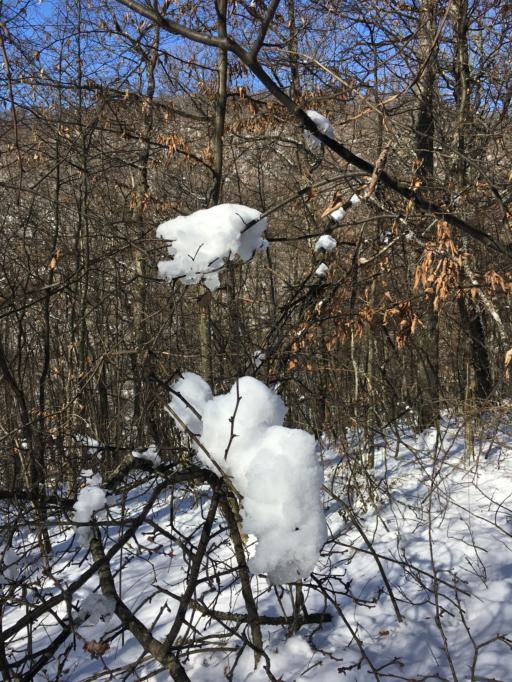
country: XK
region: Pristina
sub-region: Komuna e Prishtines
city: Pristina
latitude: 42.6732
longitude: 21.2217
